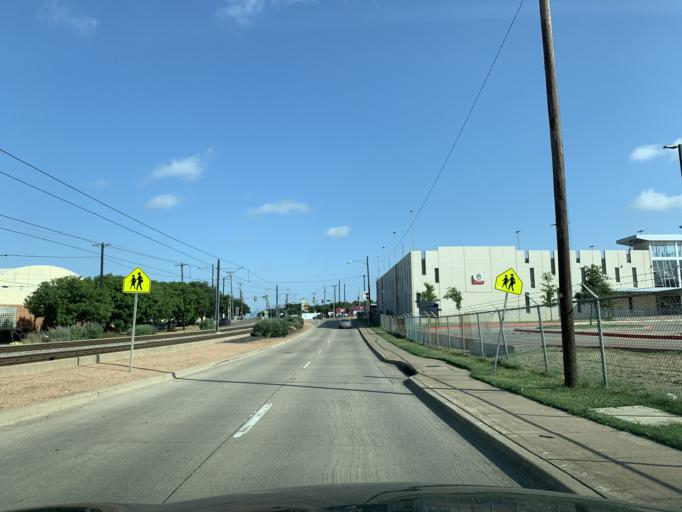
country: US
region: Texas
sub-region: Dallas County
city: Dallas
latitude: 32.6955
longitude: -96.7936
